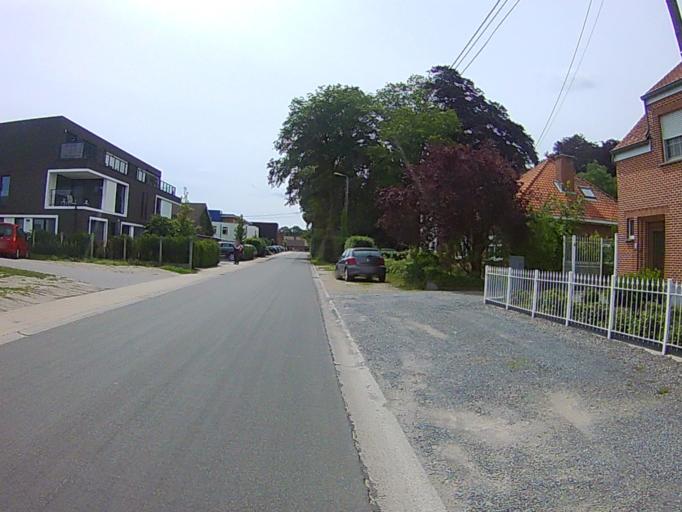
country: BE
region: Flanders
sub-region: Provincie Vlaams-Brabant
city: Keerbergen
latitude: 51.0017
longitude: 4.6289
